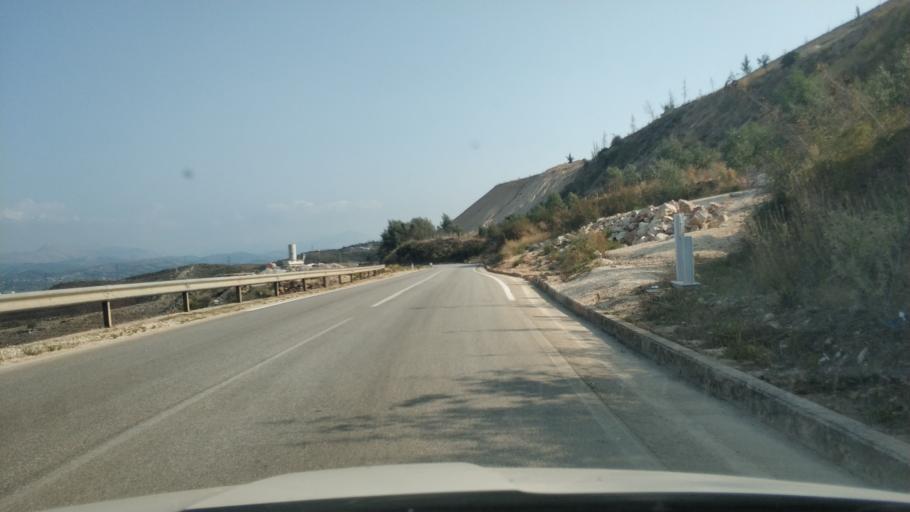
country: AL
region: Vlore
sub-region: Rrethi i Sarandes
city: Sarande
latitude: 39.8918
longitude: 20.0140
